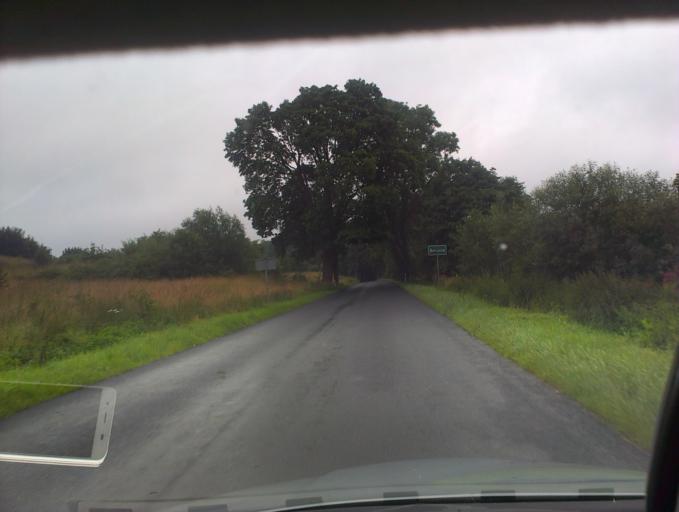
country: PL
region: West Pomeranian Voivodeship
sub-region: Powiat szczecinecki
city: Barwice
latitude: 53.7562
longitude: 16.3655
